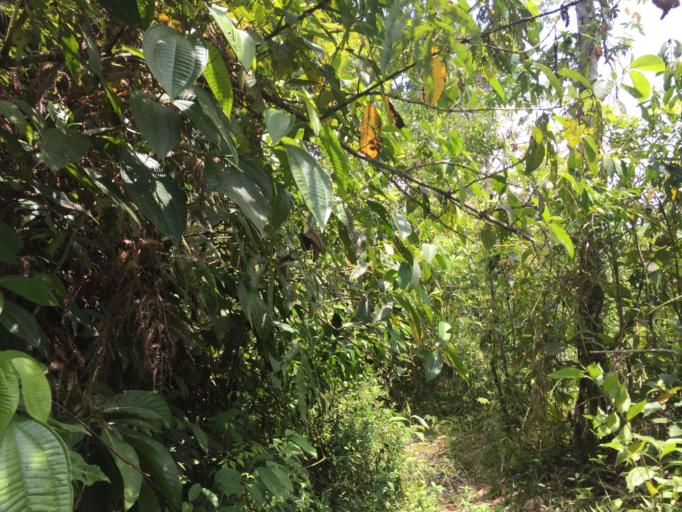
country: PE
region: Cusco
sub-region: Provincia de Paucartambo
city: Pillcopata
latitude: -12.7972
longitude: -71.3951
